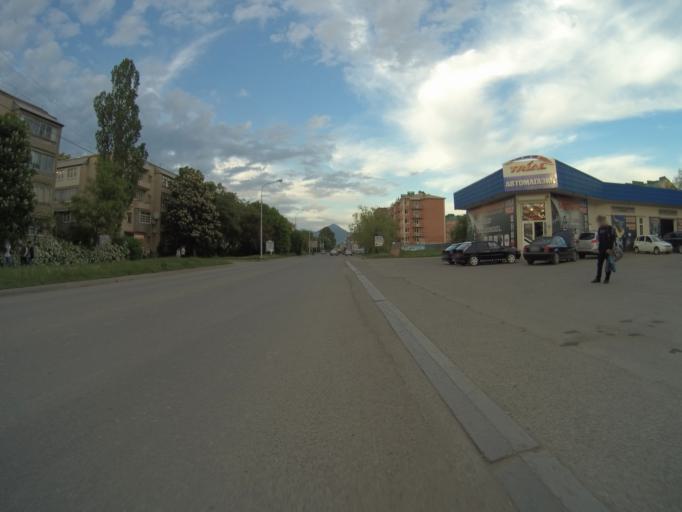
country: RU
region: Stavropol'skiy
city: Yessentukskaya
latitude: 44.0443
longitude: 42.8903
